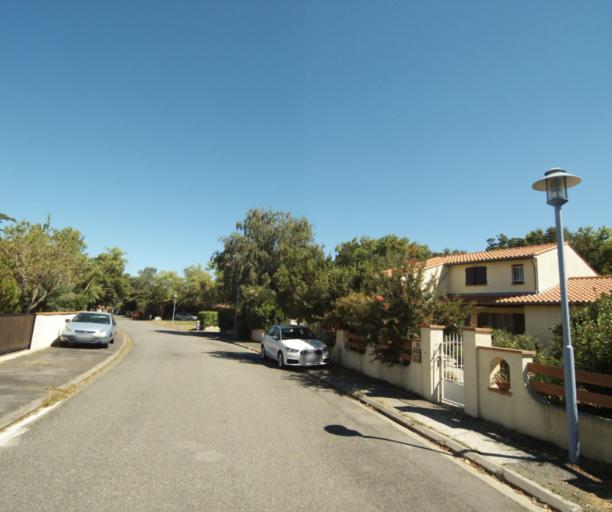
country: FR
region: Midi-Pyrenees
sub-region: Departement de la Haute-Garonne
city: Pechabou
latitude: 43.5087
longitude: 1.5170
